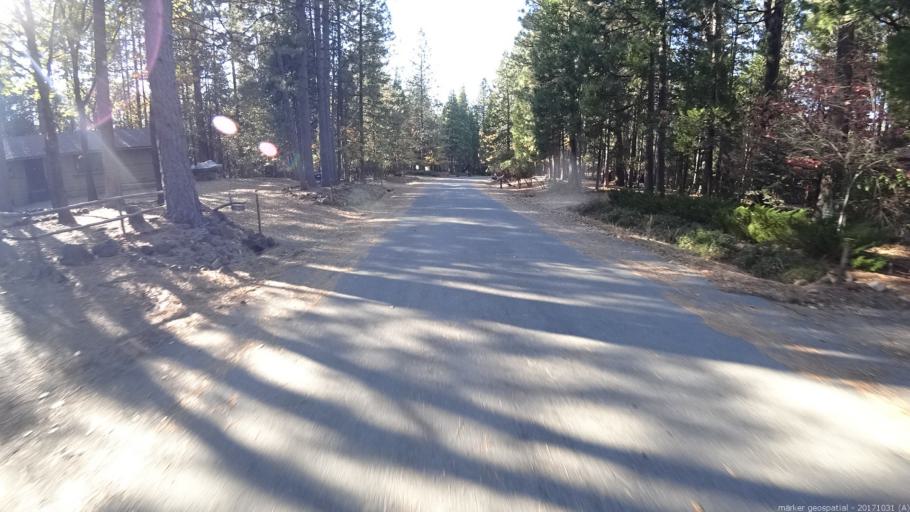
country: US
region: California
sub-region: Shasta County
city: Shingletown
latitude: 40.5016
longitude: -121.9136
